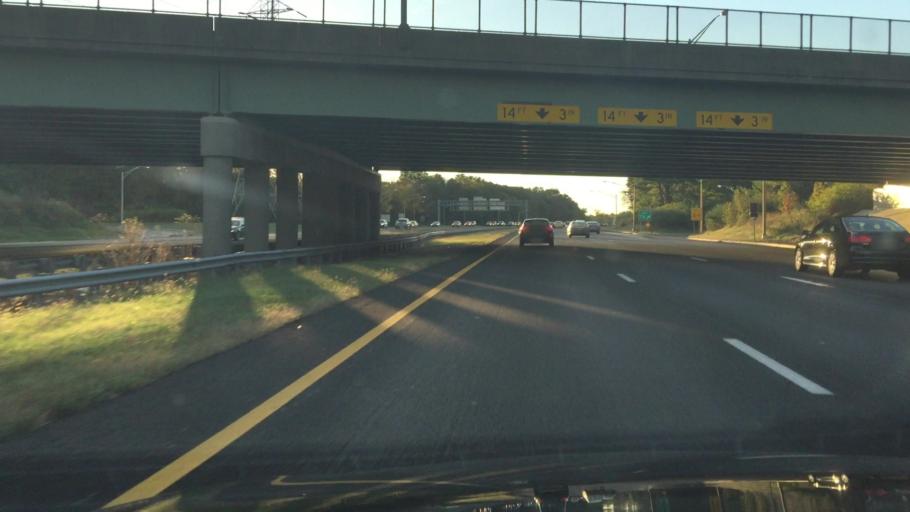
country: US
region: New Jersey
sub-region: Mercer County
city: Lawrenceville
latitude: 40.2858
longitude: -74.7320
